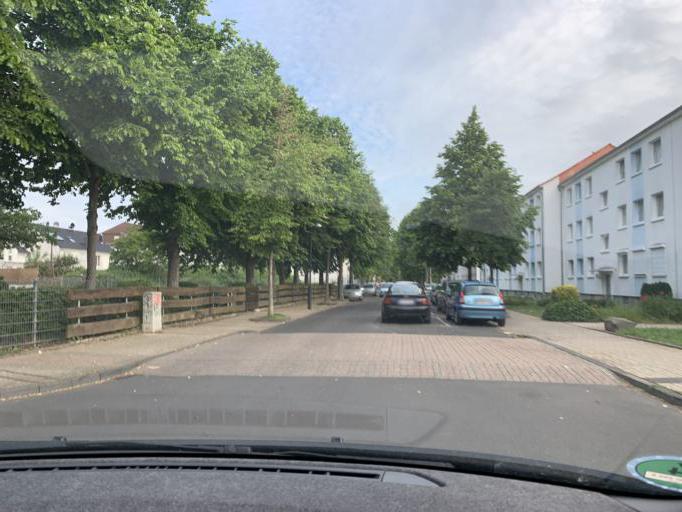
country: DE
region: North Rhine-Westphalia
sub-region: Regierungsbezirk Koln
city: Dueren
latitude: 50.7998
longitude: 6.5039
